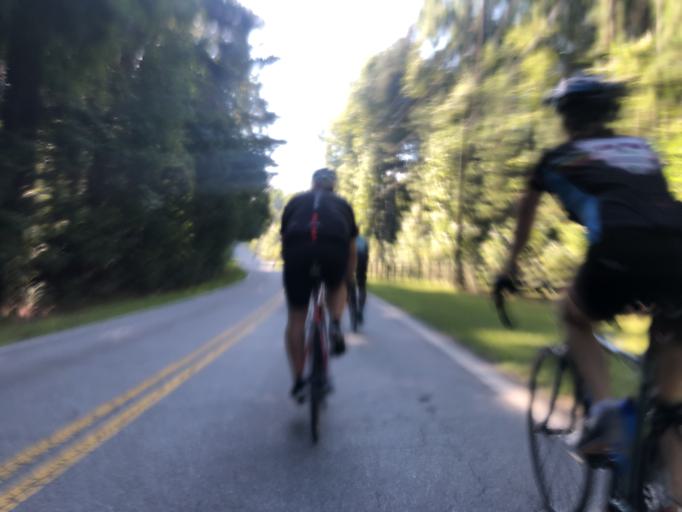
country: US
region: Georgia
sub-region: Fulton County
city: Chattahoochee Hills
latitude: 33.5506
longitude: -84.7670
